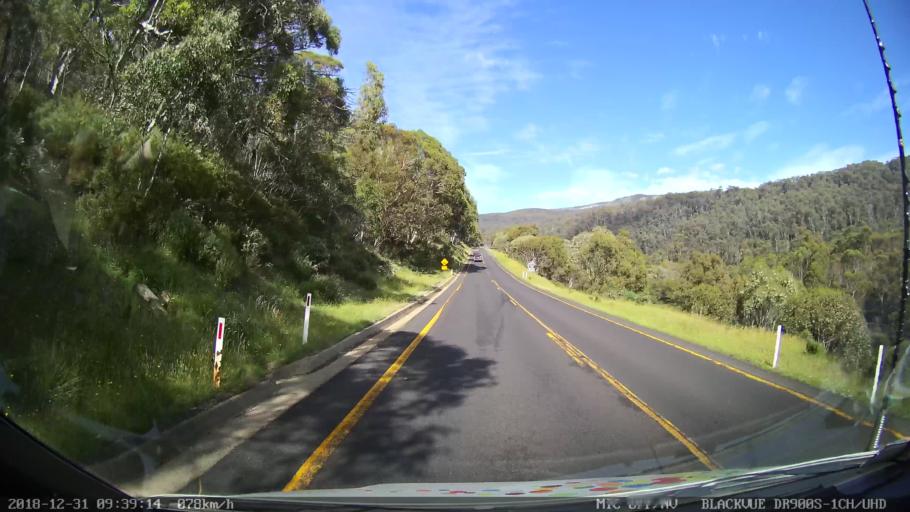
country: AU
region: New South Wales
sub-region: Snowy River
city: Jindabyne
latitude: -36.4785
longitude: 148.3577
